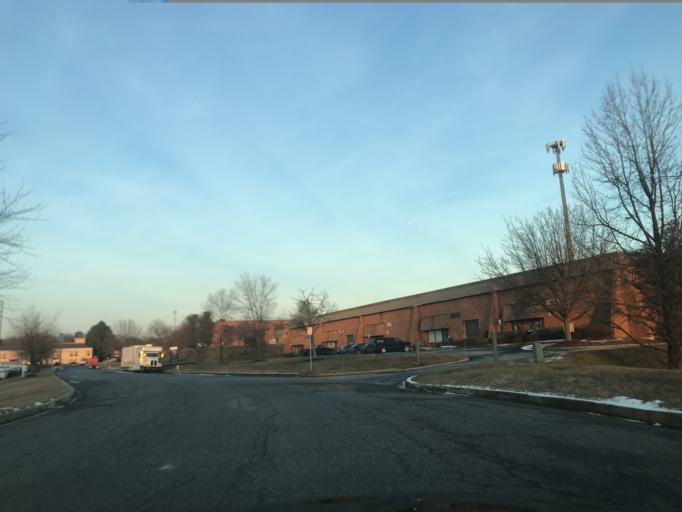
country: US
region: Maryland
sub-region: Harford County
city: Edgewood
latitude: 39.4513
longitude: -76.3121
